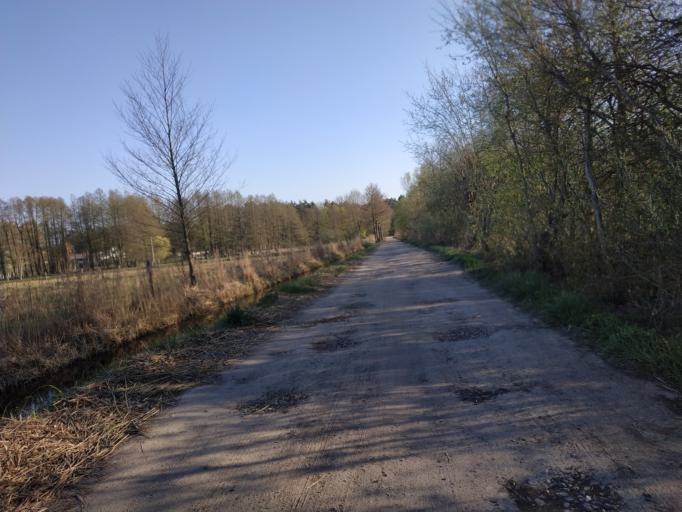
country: DE
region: Brandenburg
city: Strausberg
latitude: 52.5547
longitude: 13.8444
